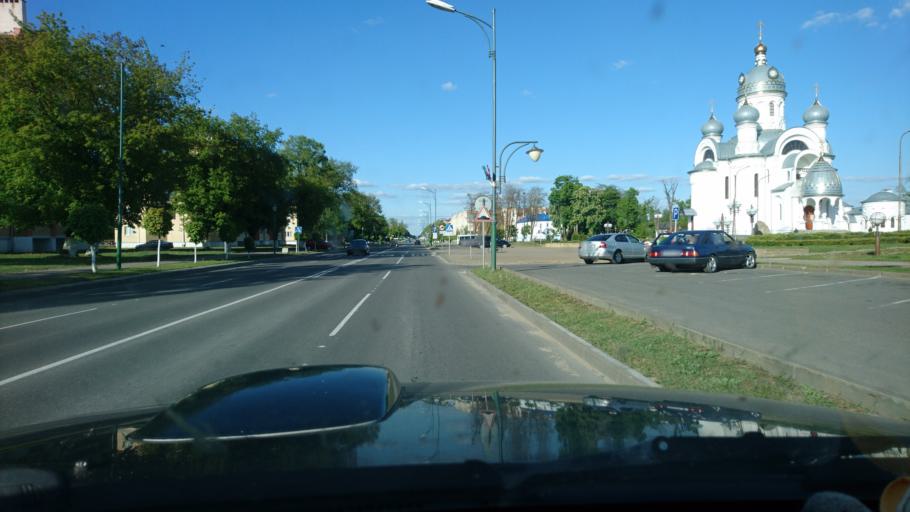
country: BY
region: Brest
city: Byaroza
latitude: 52.5251
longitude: 24.9662
